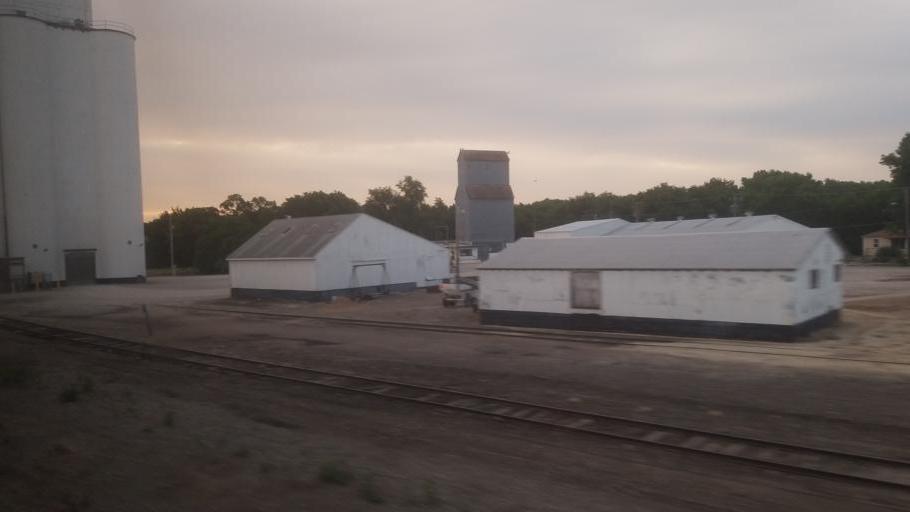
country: US
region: Kansas
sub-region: Marion County
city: Peabody
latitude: 38.1644
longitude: -97.1058
